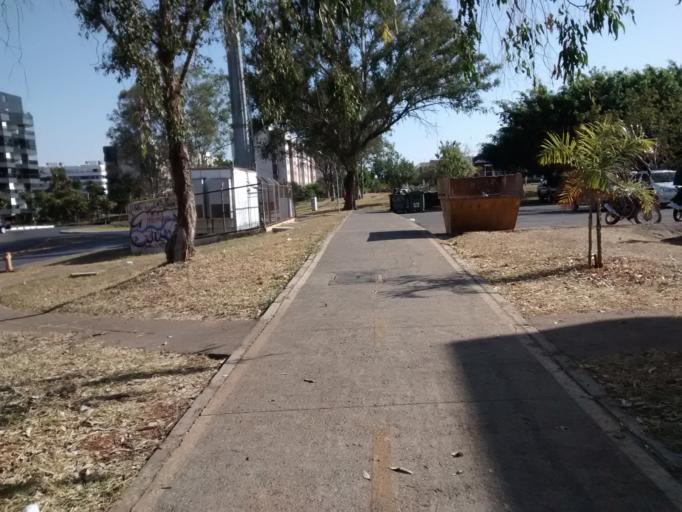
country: BR
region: Federal District
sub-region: Brasilia
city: Brasilia
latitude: -15.8021
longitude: -47.9261
